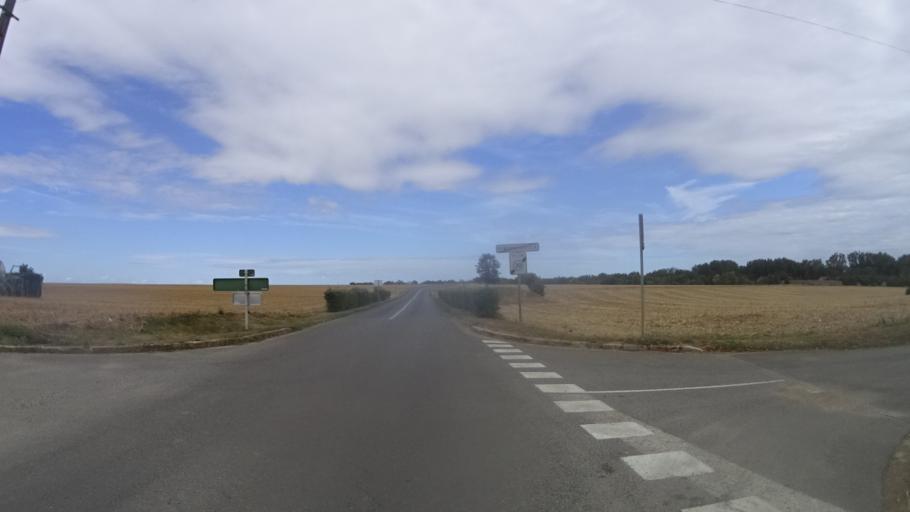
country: FR
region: Centre
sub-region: Departement du Loiret
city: Malesherbes
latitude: 48.2360
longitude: 2.4304
